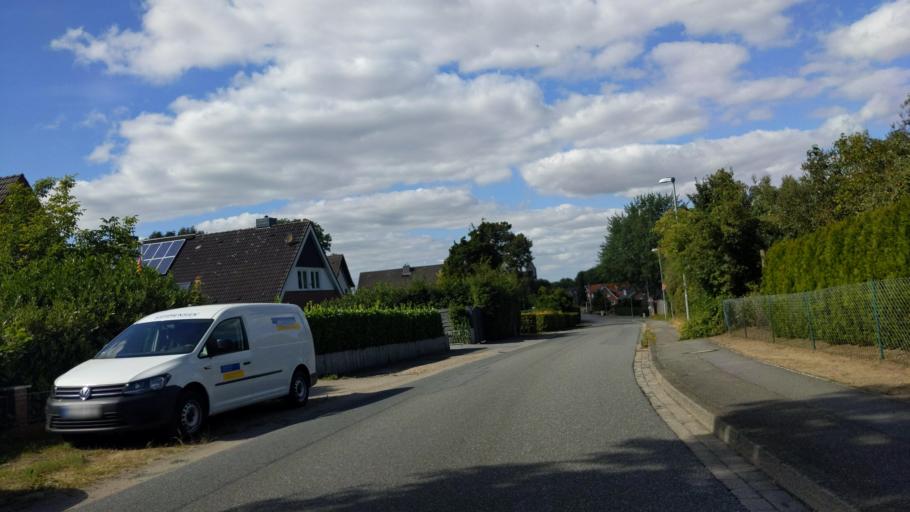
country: DE
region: Schleswig-Holstein
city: Monkhagen
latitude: 53.9343
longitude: 10.6007
